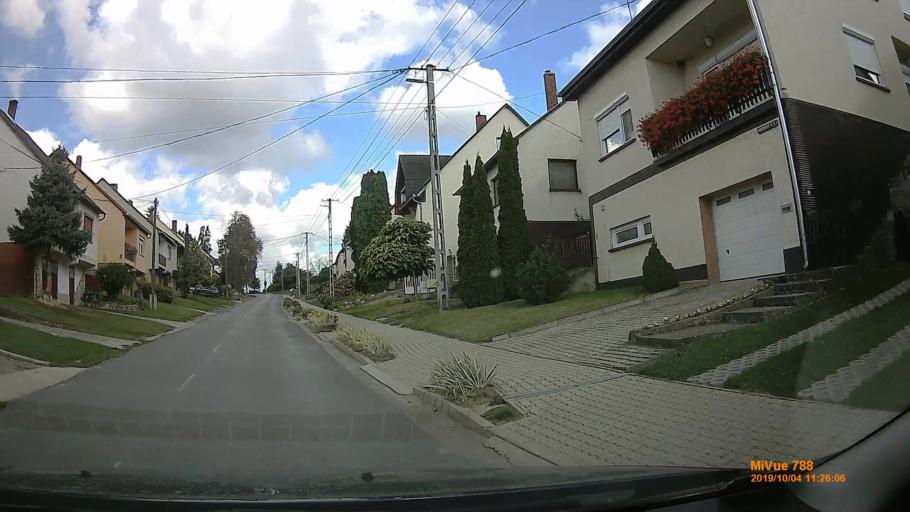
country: HU
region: Somogy
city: Kaposvar
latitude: 46.5073
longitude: 17.8159
